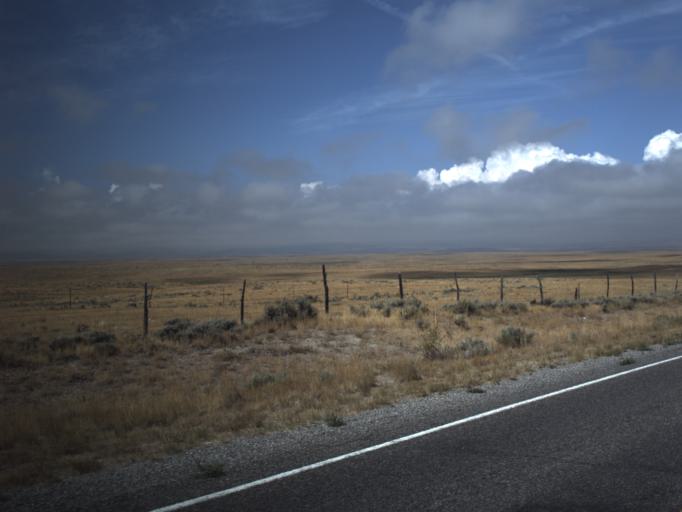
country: US
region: Wyoming
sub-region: Uinta County
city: Evanston
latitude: 41.4472
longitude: -111.0818
